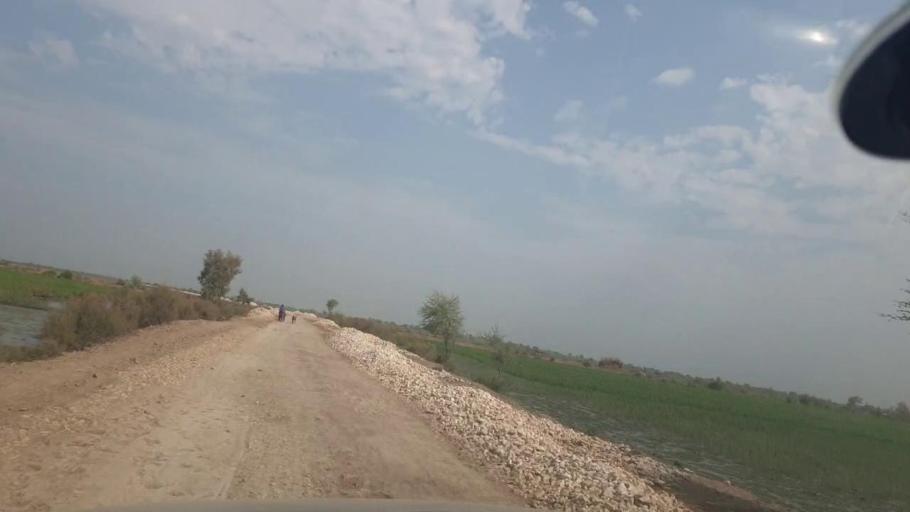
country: PK
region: Balochistan
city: Mehrabpur
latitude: 28.0775
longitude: 68.1012
